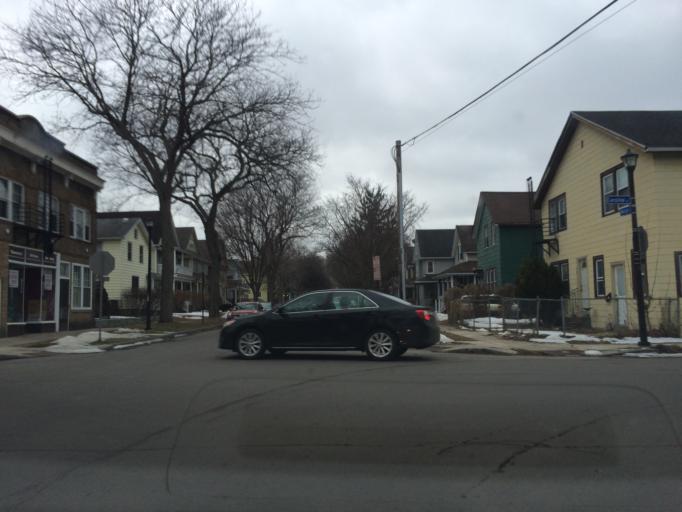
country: US
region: New York
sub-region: Monroe County
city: Rochester
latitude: 43.1391
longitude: -77.5998
